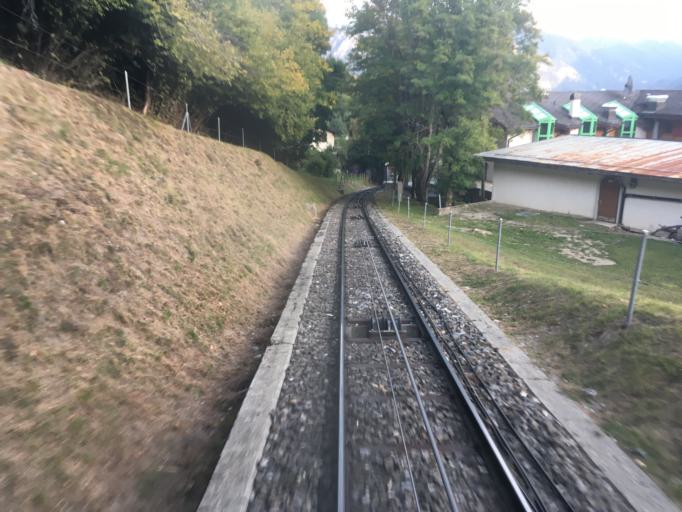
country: CH
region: Valais
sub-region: Sierre District
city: Randogne
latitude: 46.3115
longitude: 7.4986
